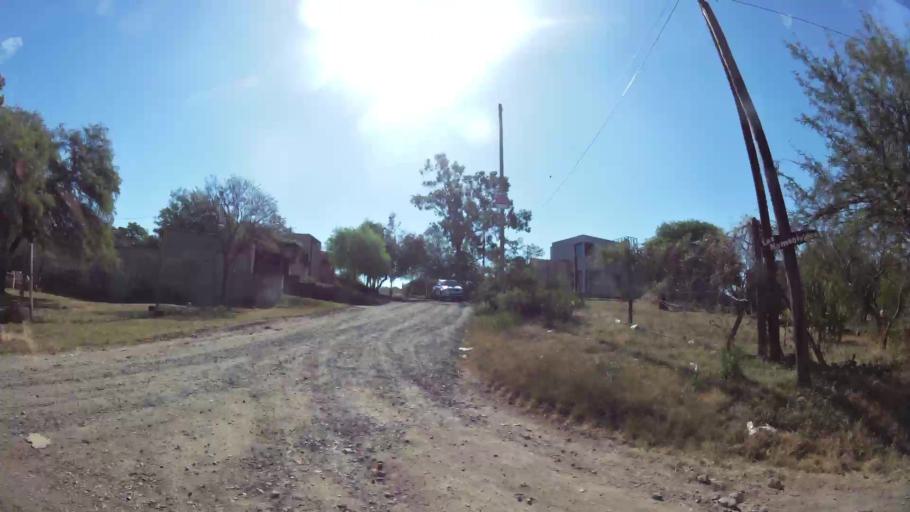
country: AR
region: Cordoba
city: La Calera
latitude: -31.3528
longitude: -64.3146
